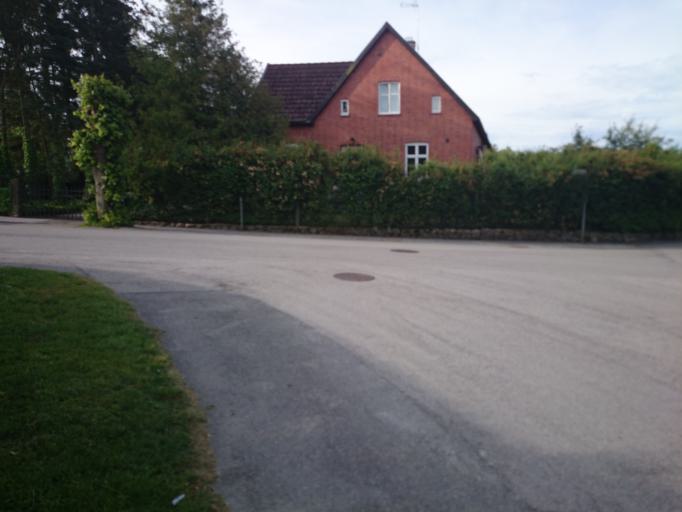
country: SE
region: Skane
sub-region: Lunds Kommun
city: Genarp
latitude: 55.7187
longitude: 13.3450
